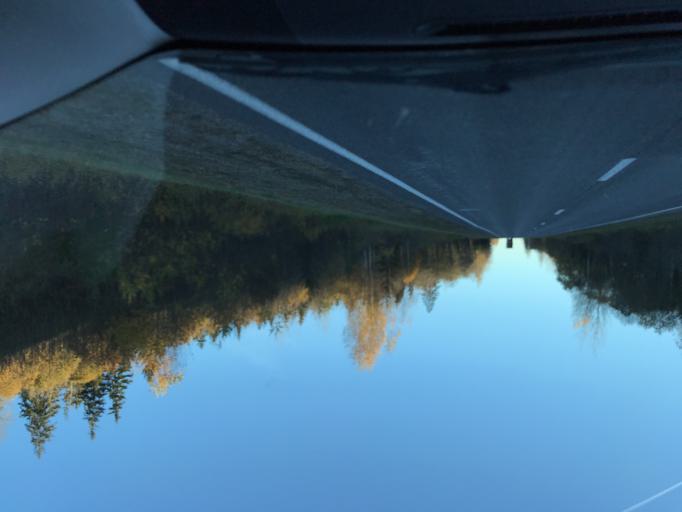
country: BY
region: Vitebsk
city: Vitebsk
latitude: 55.3461
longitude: 30.2167
